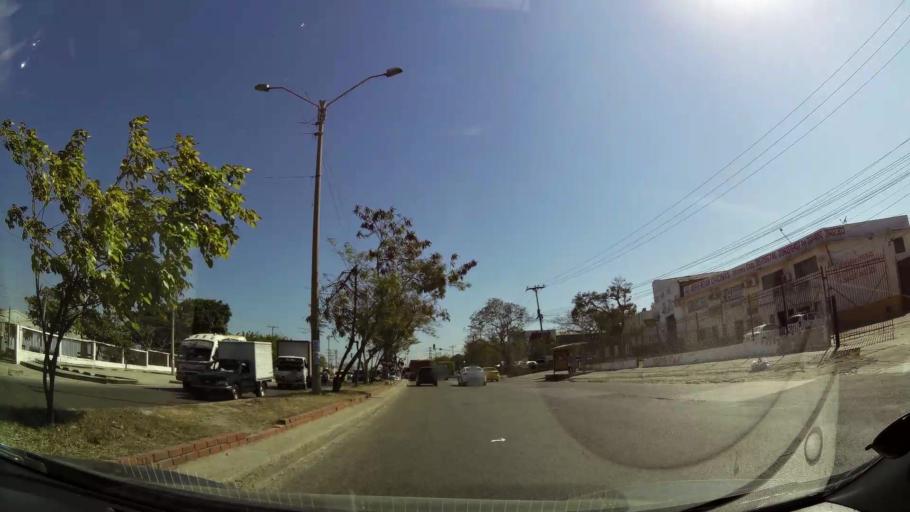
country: CO
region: Atlantico
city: Barranquilla
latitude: 10.9532
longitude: -74.7866
